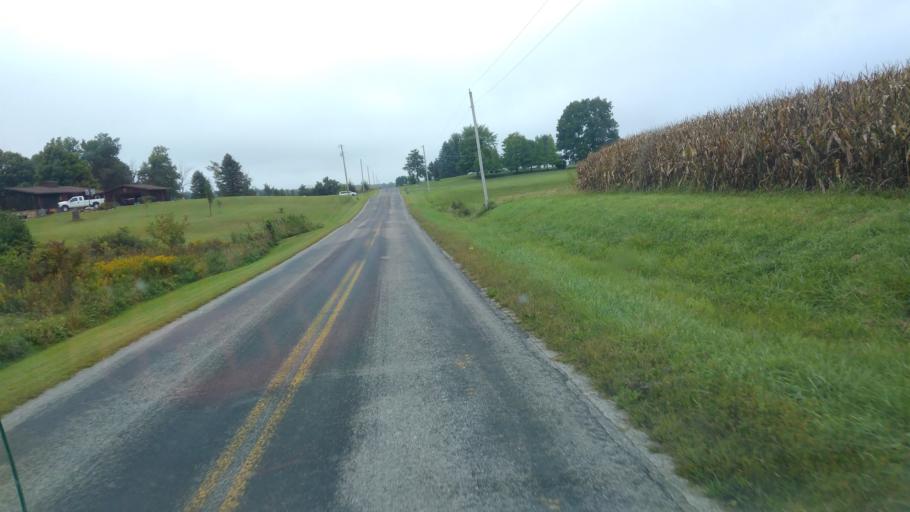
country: US
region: Ohio
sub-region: Hardin County
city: Kenton
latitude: 40.5581
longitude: -83.6361
